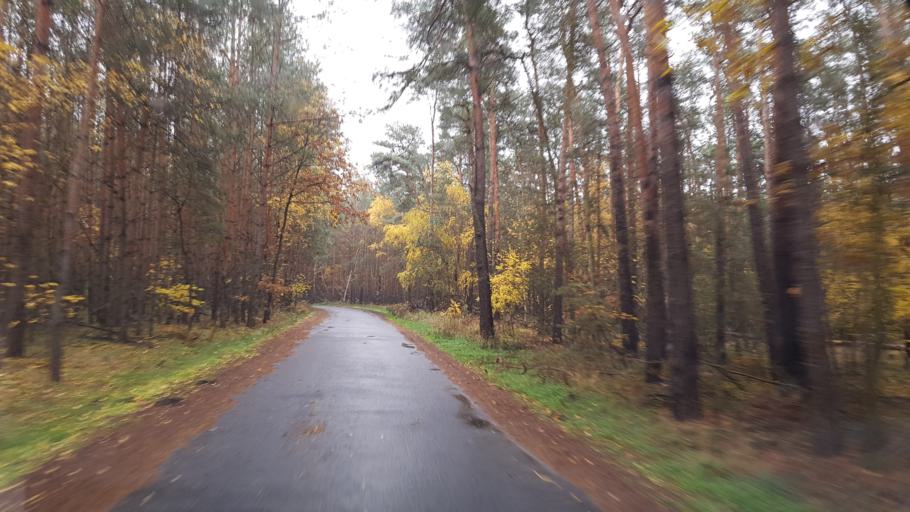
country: DE
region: Brandenburg
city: Herzberg
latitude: 51.6563
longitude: 13.2461
